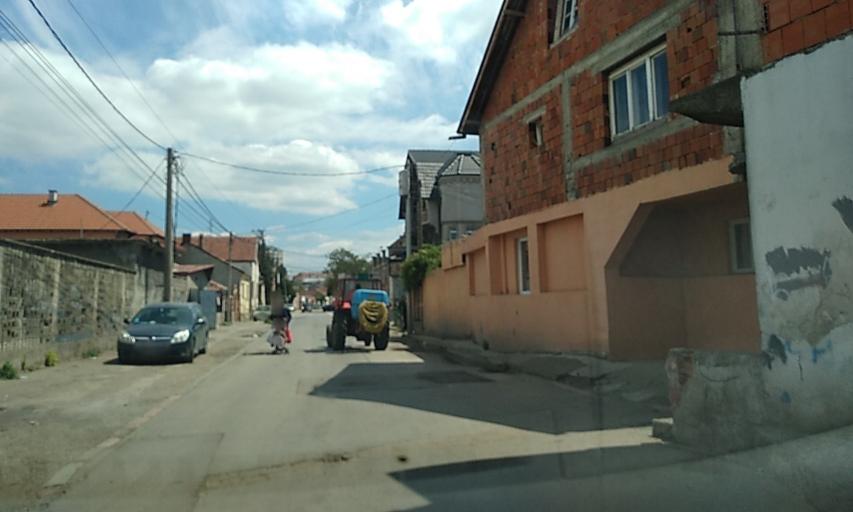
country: RS
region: Central Serbia
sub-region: Nisavski Okrug
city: Nis
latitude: 43.3217
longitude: 21.8823
